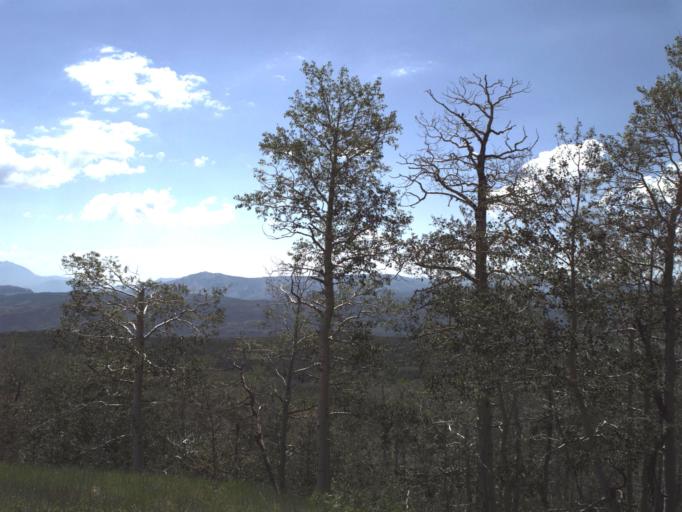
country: US
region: Utah
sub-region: Weber County
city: Wolf Creek
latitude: 41.4186
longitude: -111.5222
